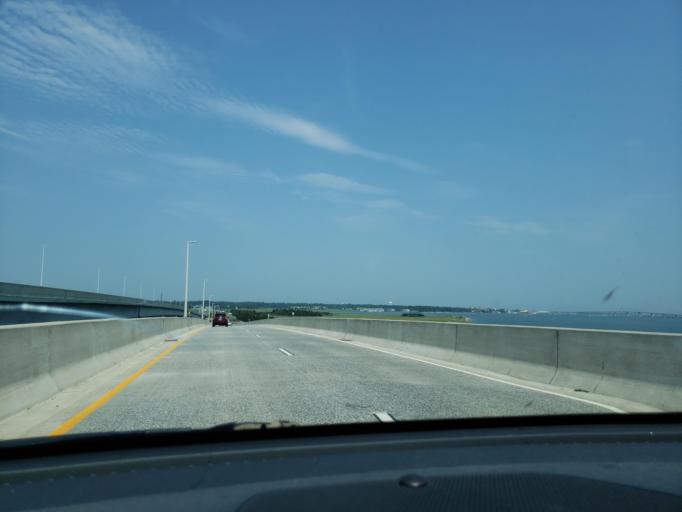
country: US
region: New Jersey
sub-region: Atlantic County
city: Somers Point
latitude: 39.2923
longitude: -74.6227
